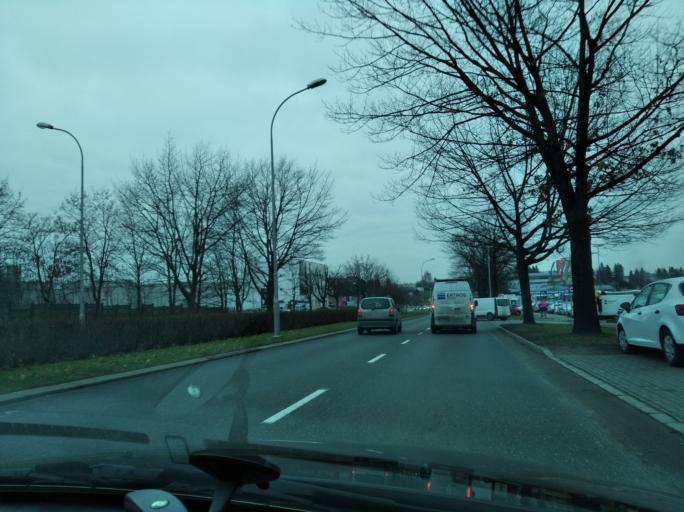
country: PL
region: Subcarpathian Voivodeship
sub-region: Rzeszow
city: Rzeszow
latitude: 50.0537
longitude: 21.9887
